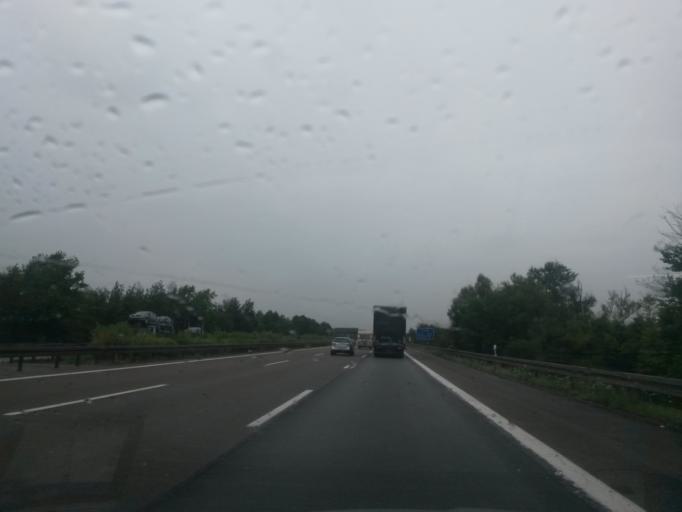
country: DE
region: Bavaria
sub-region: Upper Bavaria
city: Lenting
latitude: 48.7804
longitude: 11.4606
